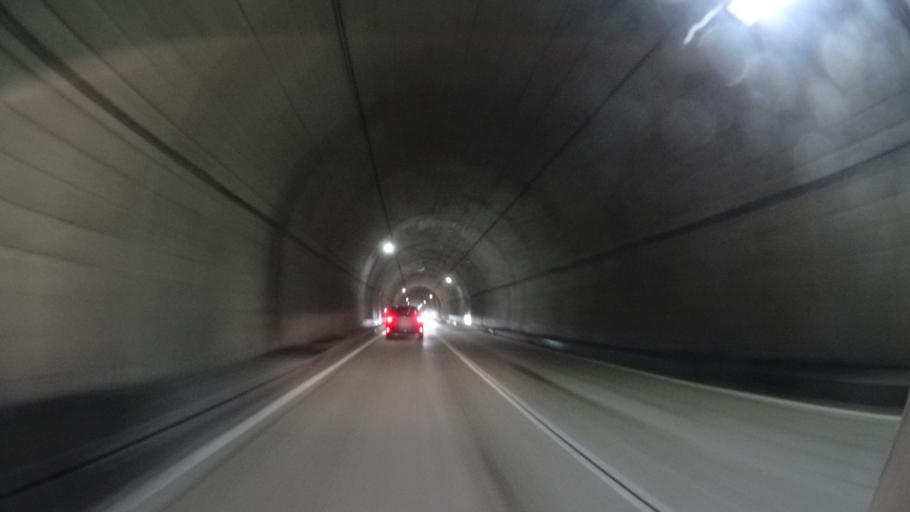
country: JP
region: Fukui
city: Ono
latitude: 35.9590
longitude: 136.6099
